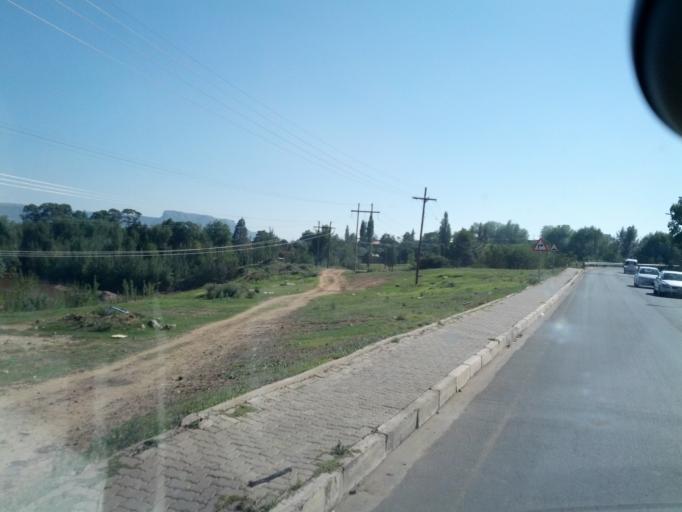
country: LS
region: Maseru
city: Maseru
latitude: -29.3014
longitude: 27.4915
